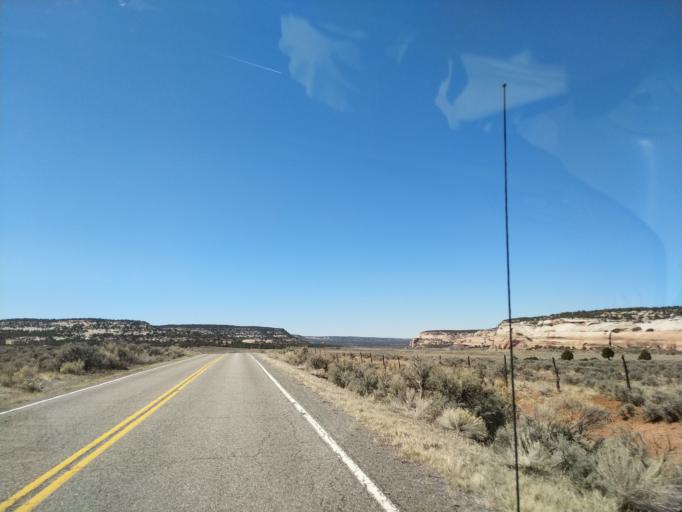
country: US
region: Colorado
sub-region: Mesa County
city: Loma
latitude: 39.0014
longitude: -108.8503
